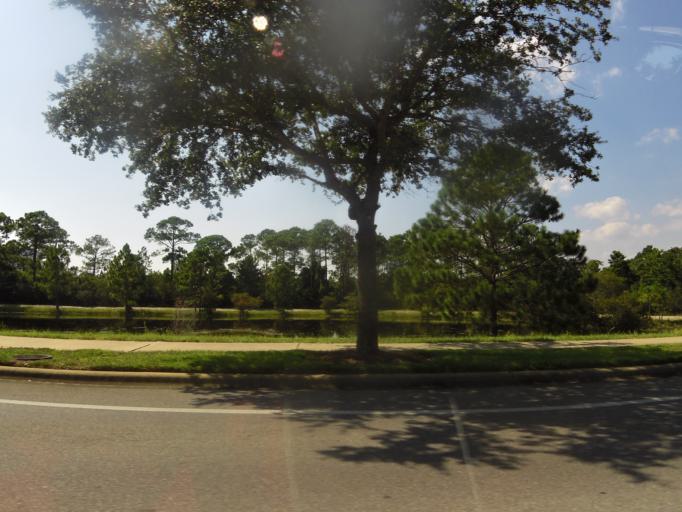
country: US
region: Florida
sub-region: Bay County
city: Laguna Beach
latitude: 30.2213
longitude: -85.8732
